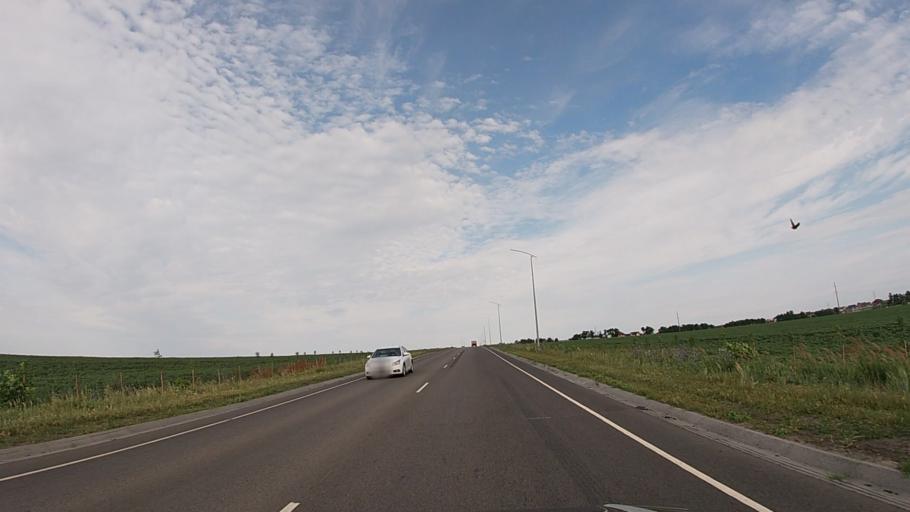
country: RU
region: Belgorod
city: Severnyy
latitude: 50.6649
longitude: 36.5109
